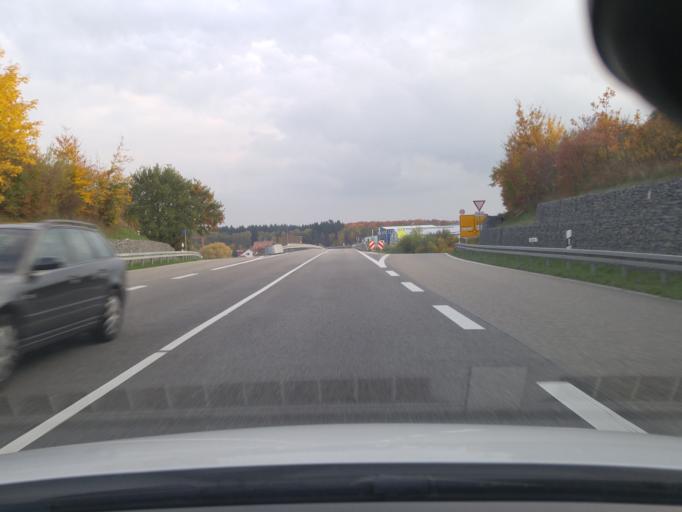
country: DE
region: Baden-Wuerttemberg
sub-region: Karlsruhe Region
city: Muhlhausen
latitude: 49.2517
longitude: 8.7104
